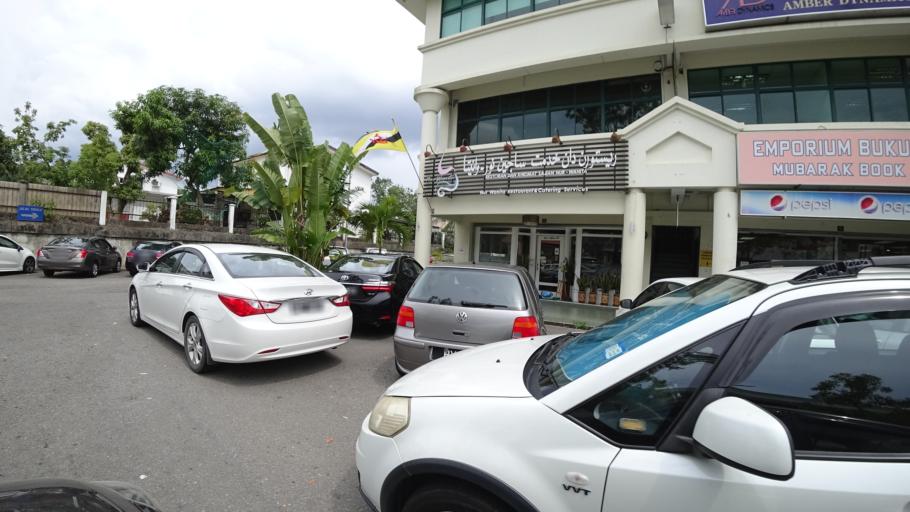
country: BN
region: Brunei and Muara
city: Bandar Seri Begawan
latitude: 4.8965
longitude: 114.9212
